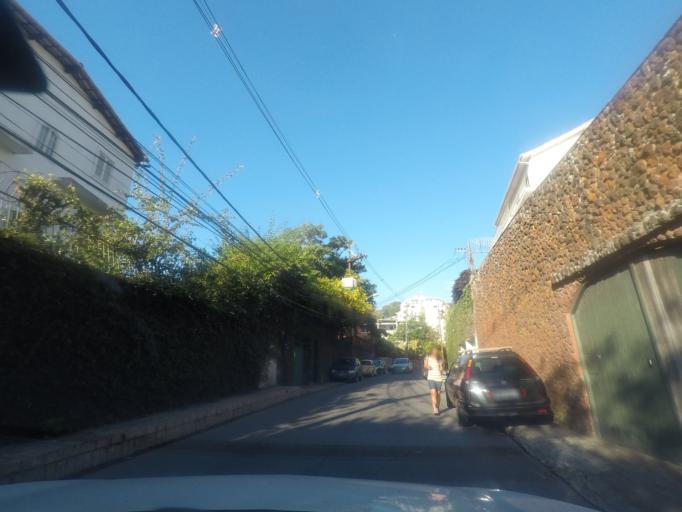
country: BR
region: Rio de Janeiro
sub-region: Rio De Janeiro
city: Rio de Janeiro
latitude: -22.9349
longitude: -43.1988
